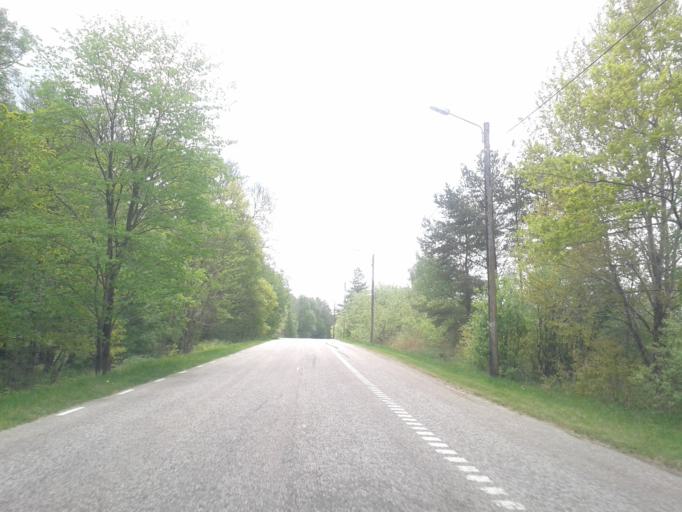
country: SE
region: Vaestra Goetaland
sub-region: Kungalvs Kommun
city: Kungalv
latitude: 57.8890
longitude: 11.9917
